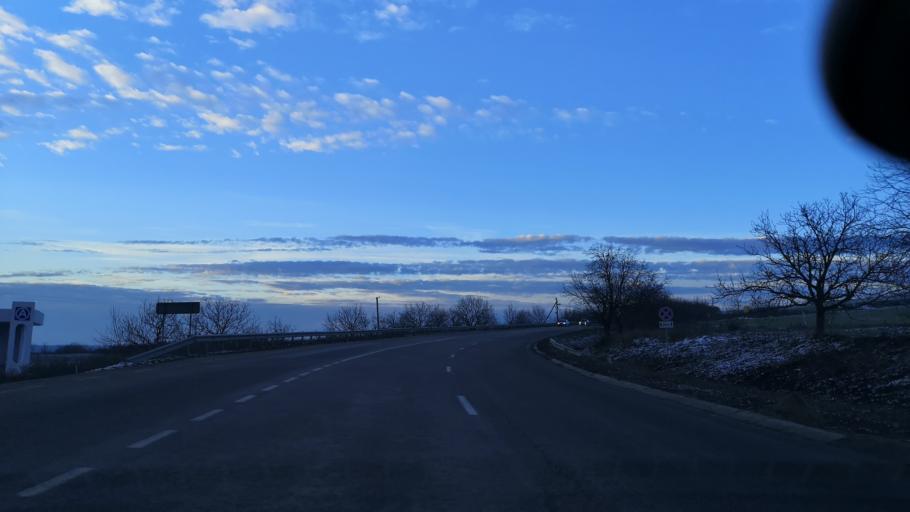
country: MD
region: Orhei
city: Orhei
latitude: 47.5244
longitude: 28.7972
